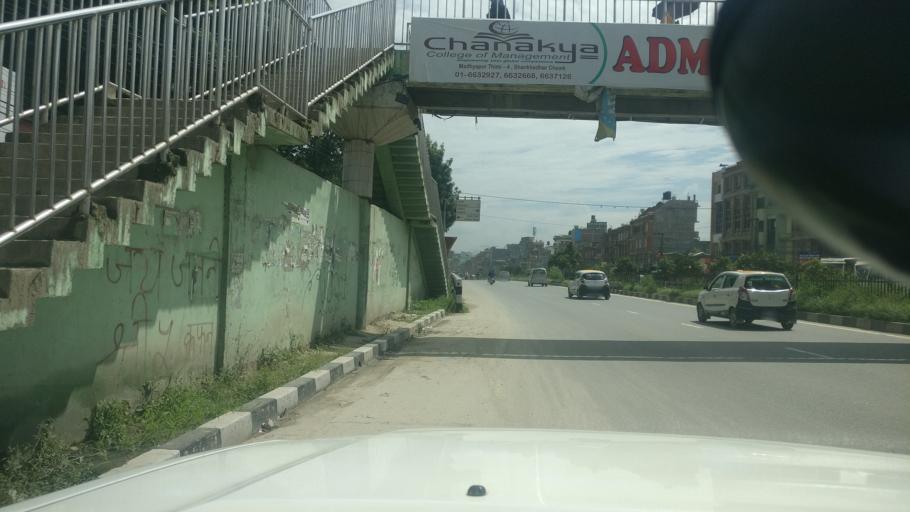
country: NP
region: Central Region
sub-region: Bagmati Zone
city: Bhaktapur
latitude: 27.6735
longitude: 85.3819
